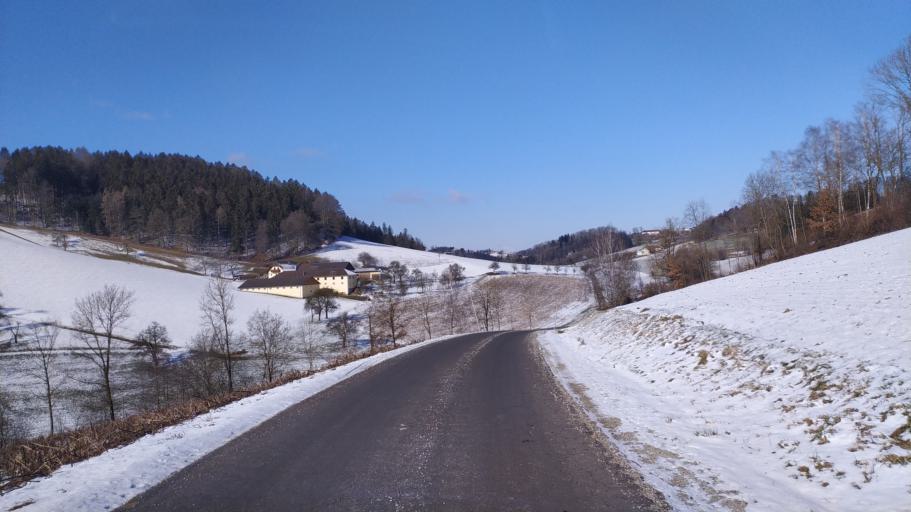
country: AT
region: Upper Austria
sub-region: Politischer Bezirk Urfahr-Umgebung
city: Ottensheim
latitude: 48.3359
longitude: 14.2244
